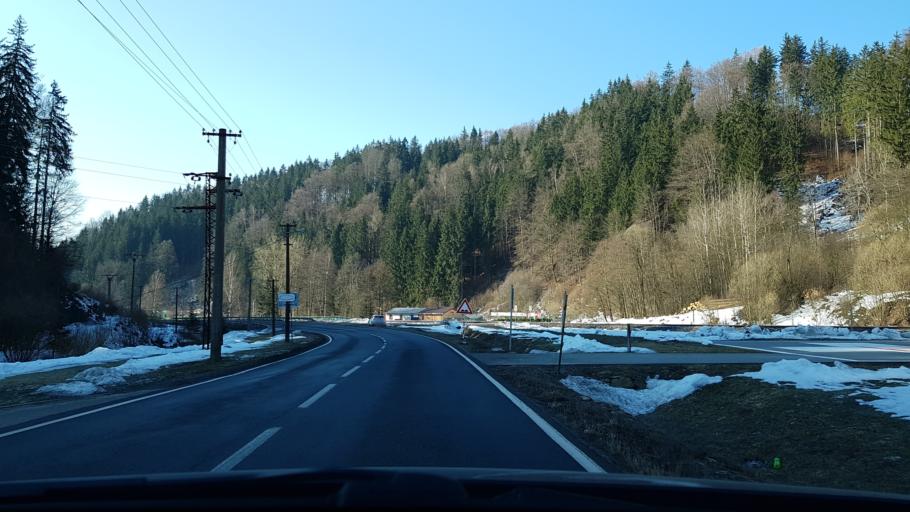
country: CZ
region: Olomoucky
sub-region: Okres Sumperk
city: Hanusovice
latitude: 50.1073
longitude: 16.9962
